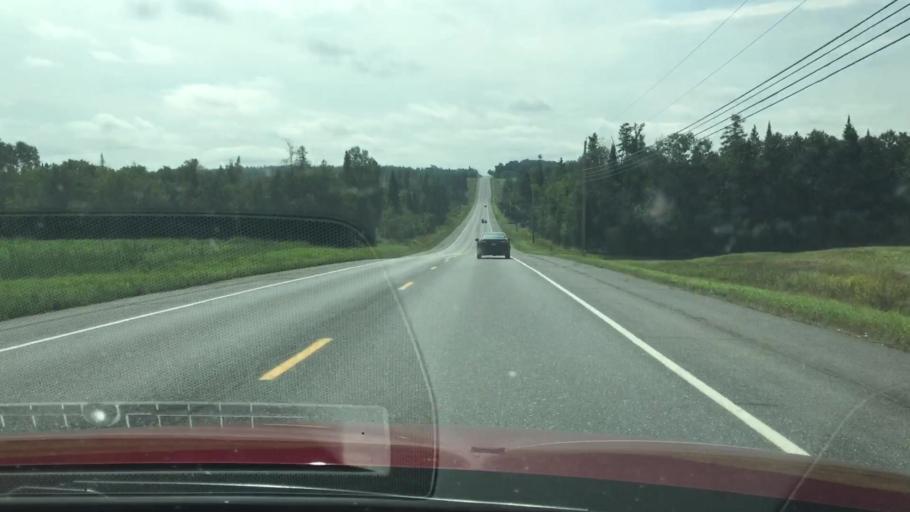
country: CA
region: New Brunswick
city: Florenceville-Bristol
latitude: 46.4067
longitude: -67.8432
